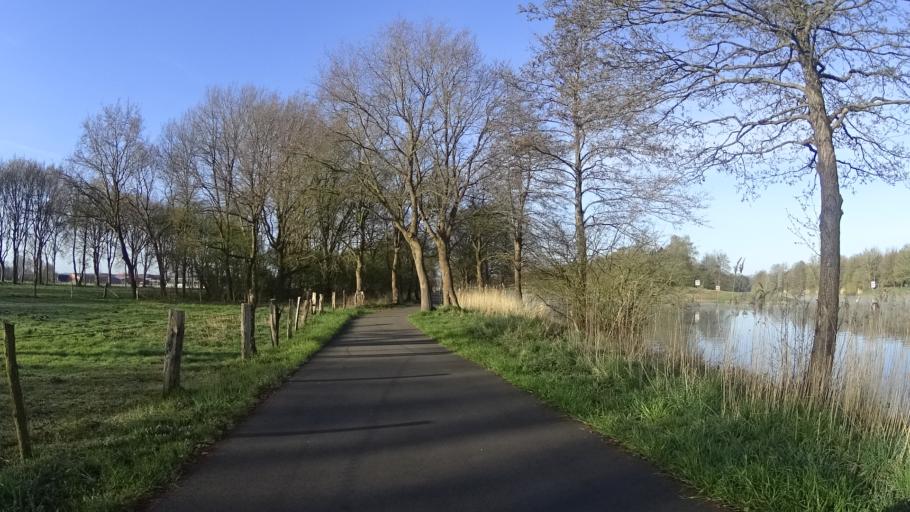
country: DE
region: Lower Saxony
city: Niederlangen
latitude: 52.8380
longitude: 7.2840
